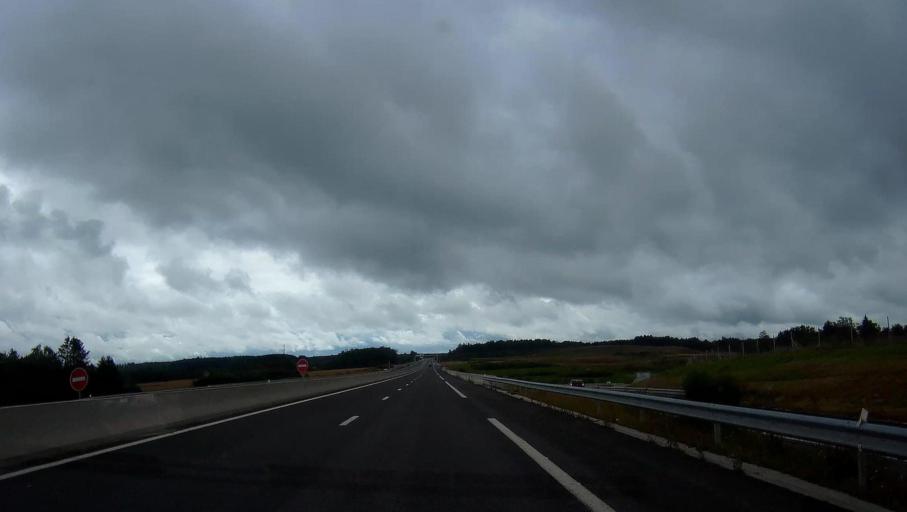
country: FR
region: Champagne-Ardenne
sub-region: Departement des Ardennes
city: Rocroi
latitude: 49.9053
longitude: 4.5219
